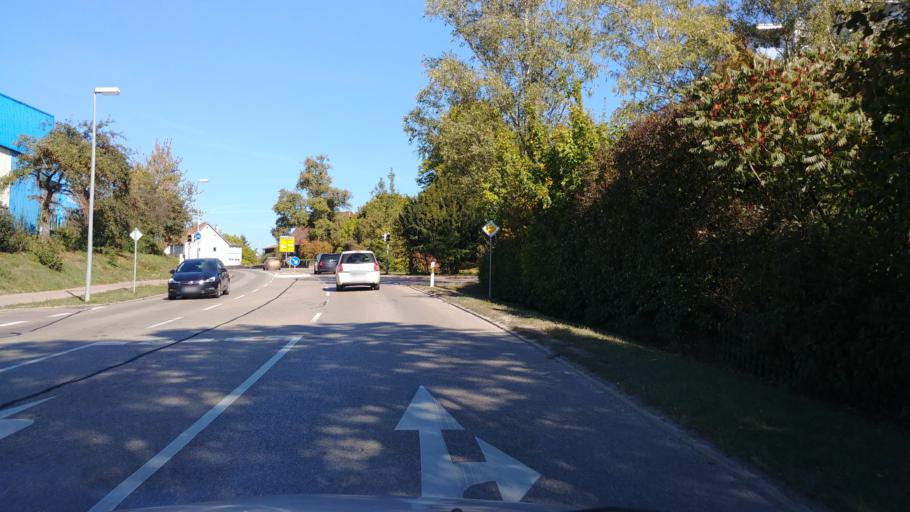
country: DE
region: Baden-Wuerttemberg
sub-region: Regierungsbezirk Stuttgart
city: Gaildorf
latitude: 48.9959
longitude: 9.7742
